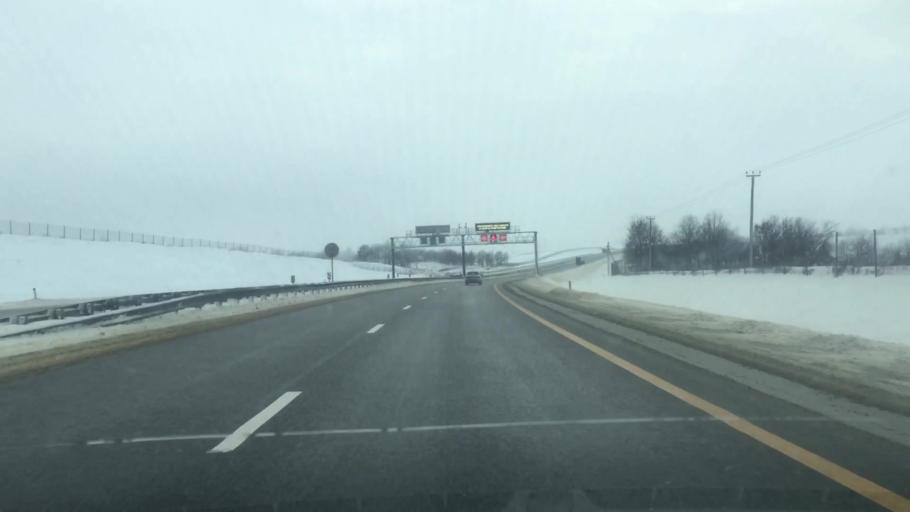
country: RU
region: Tula
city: Yefremov
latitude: 53.1377
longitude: 38.2436
